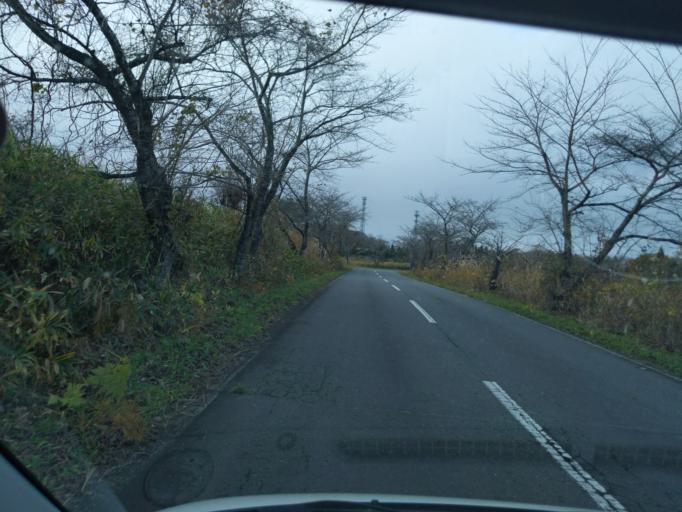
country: JP
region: Iwate
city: Mizusawa
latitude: 39.0415
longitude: 141.0772
